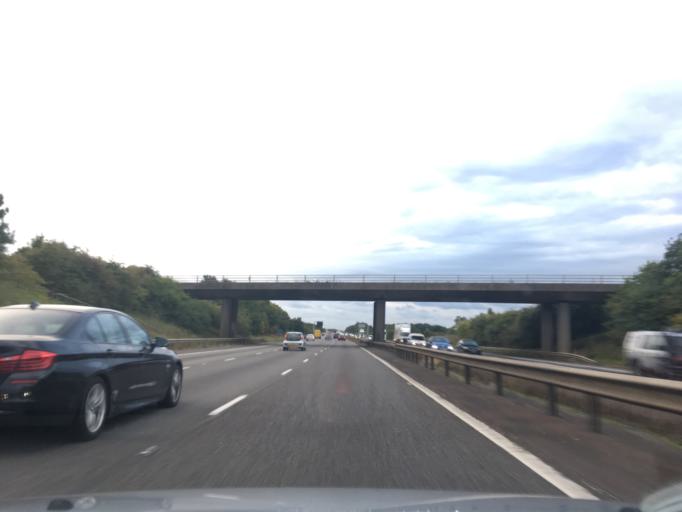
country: GB
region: England
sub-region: Oxfordshire
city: Bicester
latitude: 51.9067
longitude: -1.2057
